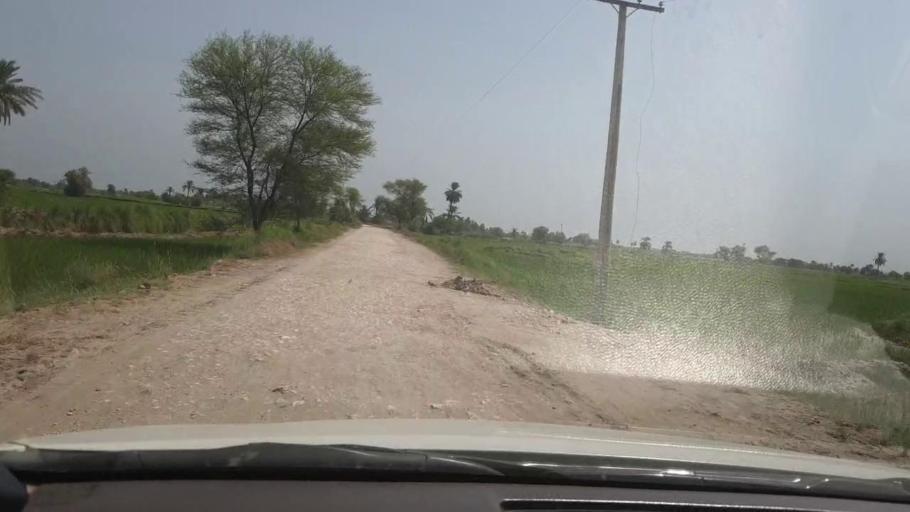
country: PK
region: Sindh
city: Shikarpur
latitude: 27.9390
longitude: 68.5992
